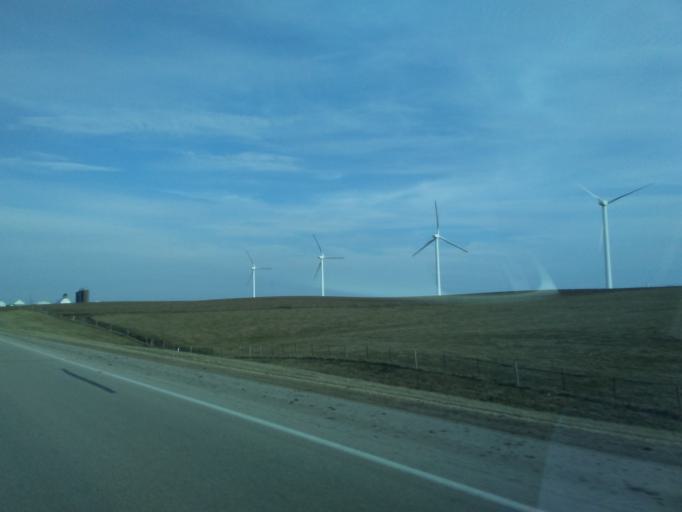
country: US
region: Wisconsin
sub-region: Iowa County
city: Mineral Point
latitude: 42.9667
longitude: -90.3766
